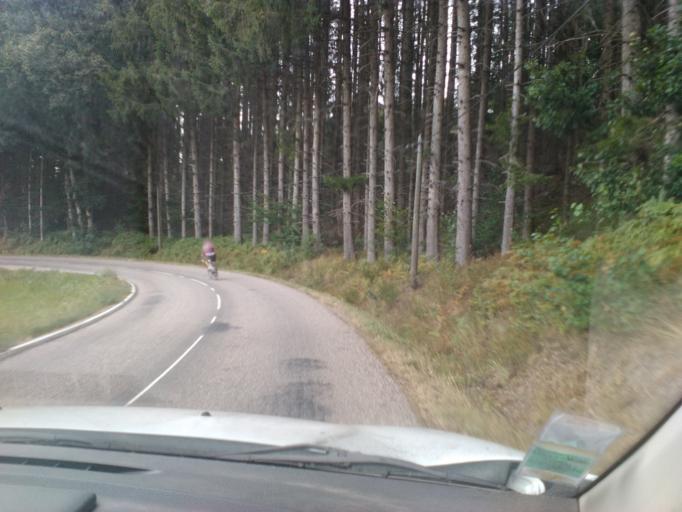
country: FR
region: Lorraine
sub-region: Departement des Vosges
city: Le Tholy
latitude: 48.1139
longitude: 6.7442
